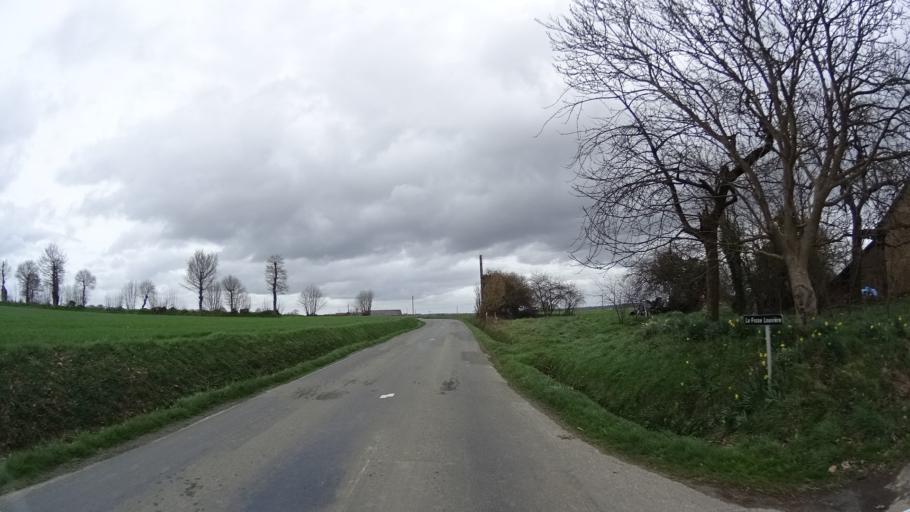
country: FR
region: Brittany
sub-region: Departement d'Ille-et-Vilaine
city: Geveze
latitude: 48.2068
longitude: -1.8283
